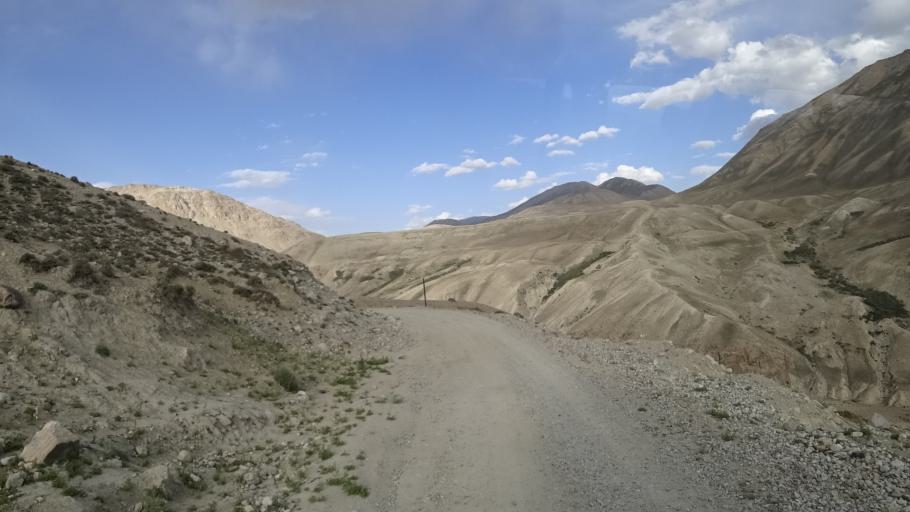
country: AF
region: Badakhshan
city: Khandud
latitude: 37.2243
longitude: 72.7995
